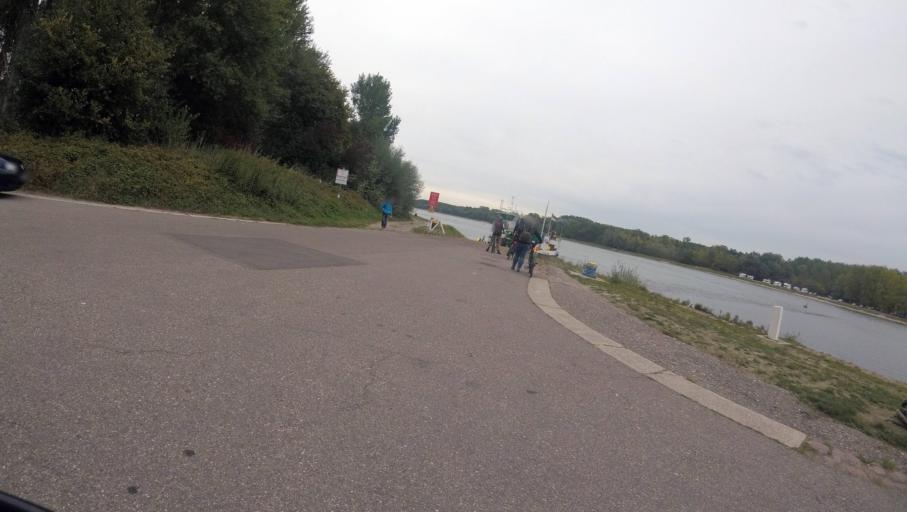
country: DE
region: Rheinland-Pfalz
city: Neuburg
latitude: 48.9788
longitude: 8.2543
